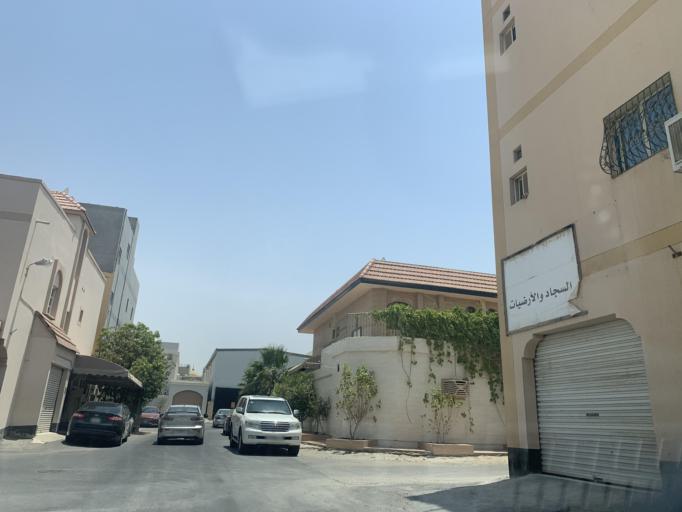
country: BH
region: Northern
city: Madinat `Isa
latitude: 26.1945
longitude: 50.4851
